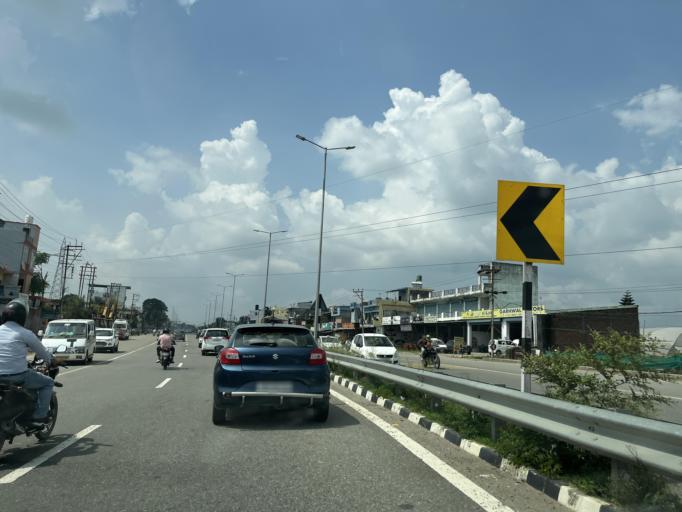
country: IN
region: Uttarakhand
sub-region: Dehradun
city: Raipur
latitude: 30.2547
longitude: 78.0934
